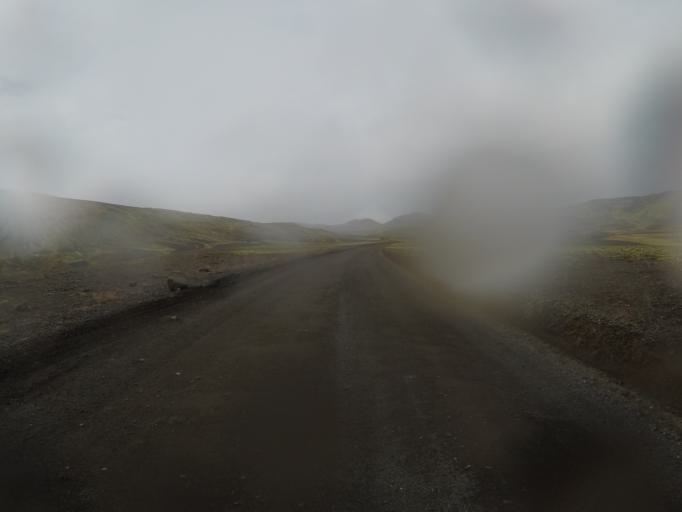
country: IS
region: South
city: Vestmannaeyjar
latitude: 63.9788
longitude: -18.8446
